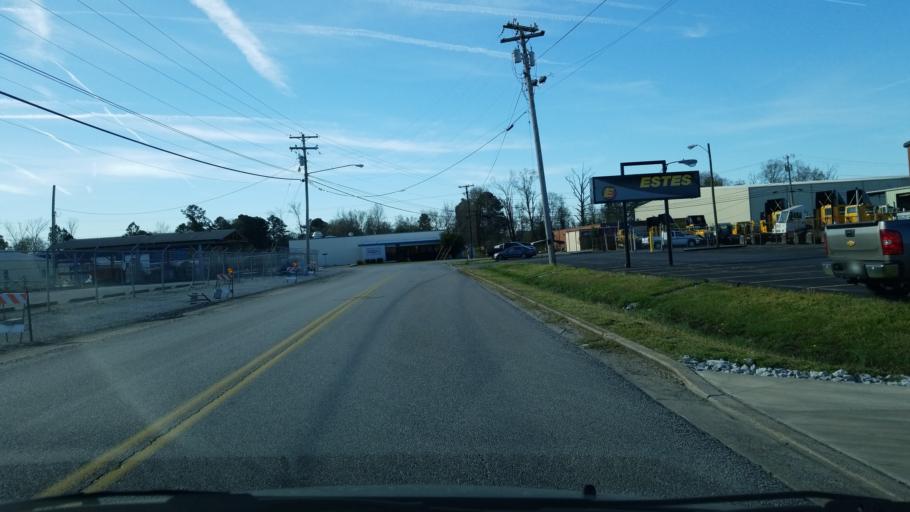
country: US
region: Tennessee
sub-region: Hamilton County
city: East Chattanooga
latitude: 35.0451
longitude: -85.1931
